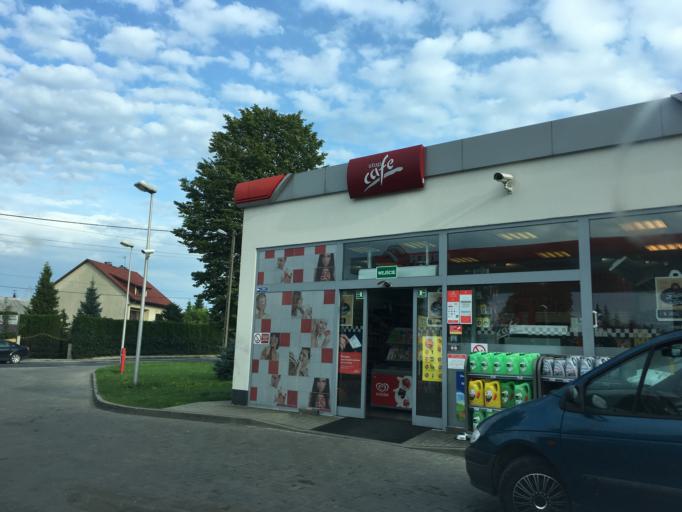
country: PL
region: Swietokrzyskie
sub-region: Powiat wloszczowski
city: Wloszczowa
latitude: 50.8433
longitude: 20.0018
